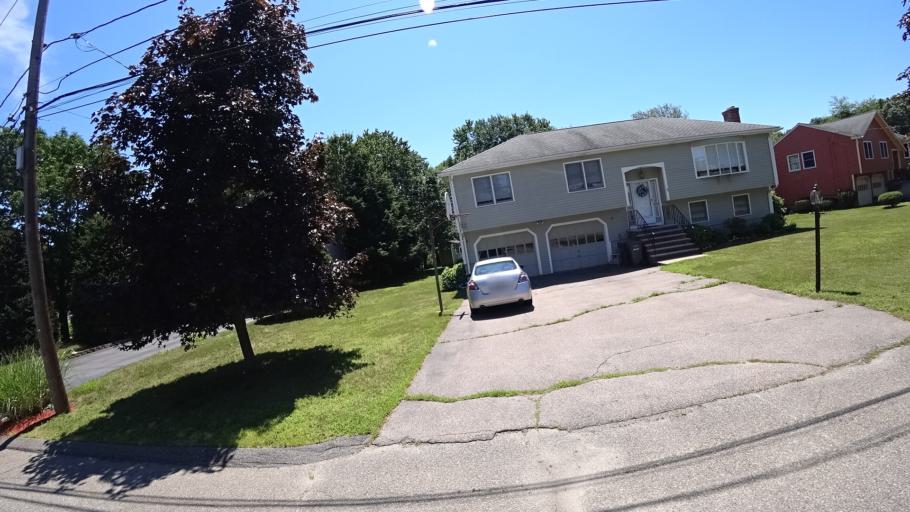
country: US
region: Massachusetts
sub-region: Norfolk County
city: Dedham
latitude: 42.2165
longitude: -71.1537
